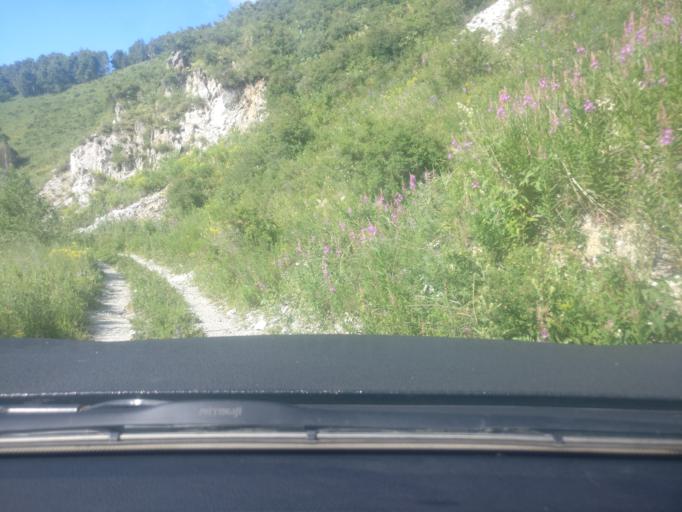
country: KZ
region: Almaty Qalasy
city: Almaty
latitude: 43.1085
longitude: 76.9327
